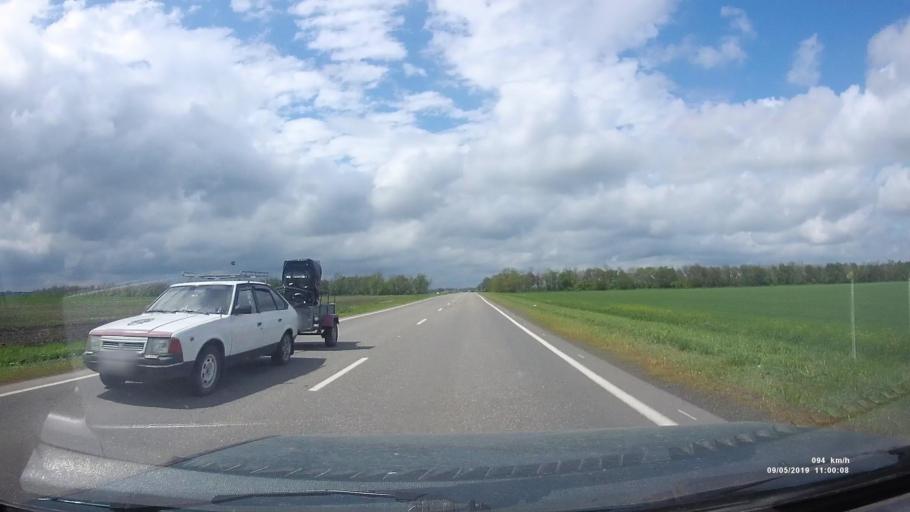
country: RU
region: Rostov
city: Peshkovo
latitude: 46.8545
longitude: 39.2262
